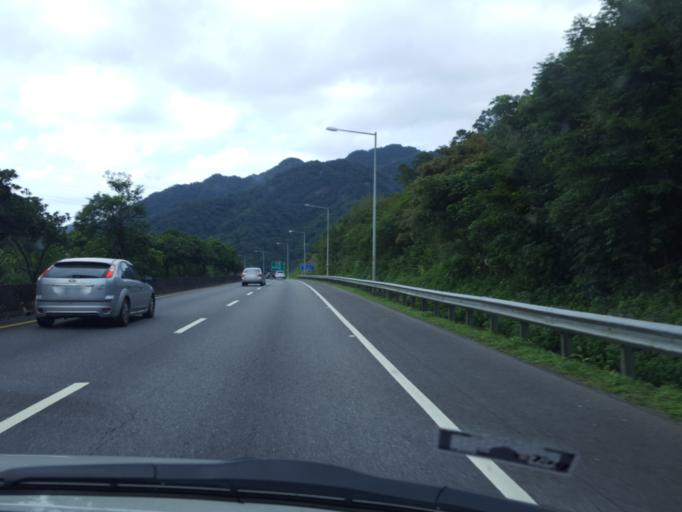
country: TW
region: Taipei
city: Taipei
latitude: 24.9759
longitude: 121.6775
